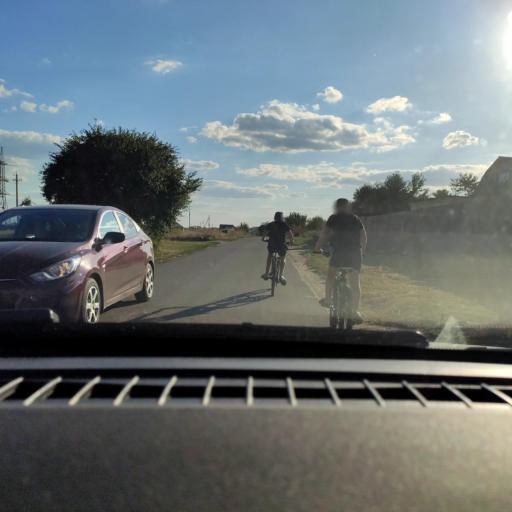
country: RU
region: Voronezj
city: Devitsa
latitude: 51.6458
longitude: 38.9458
